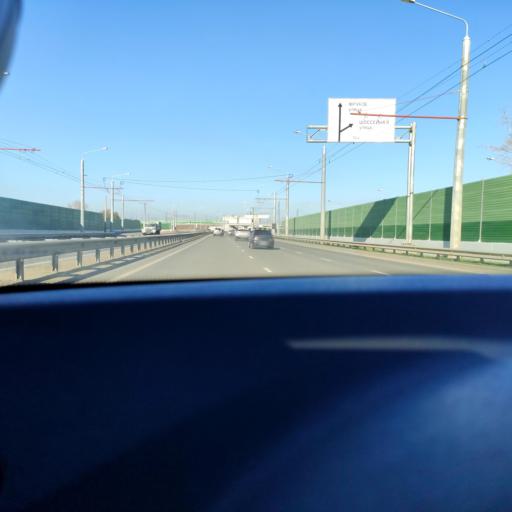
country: RU
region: Samara
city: Samara
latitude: 53.1620
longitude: 50.0884
